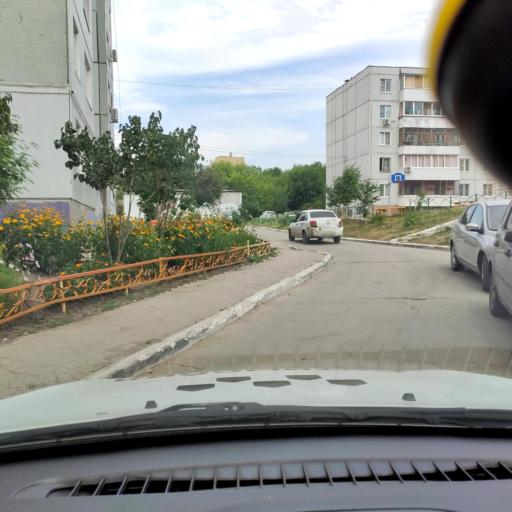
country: RU
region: Samara
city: Zhigulevsk
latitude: 53.4115
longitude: 49.5282
